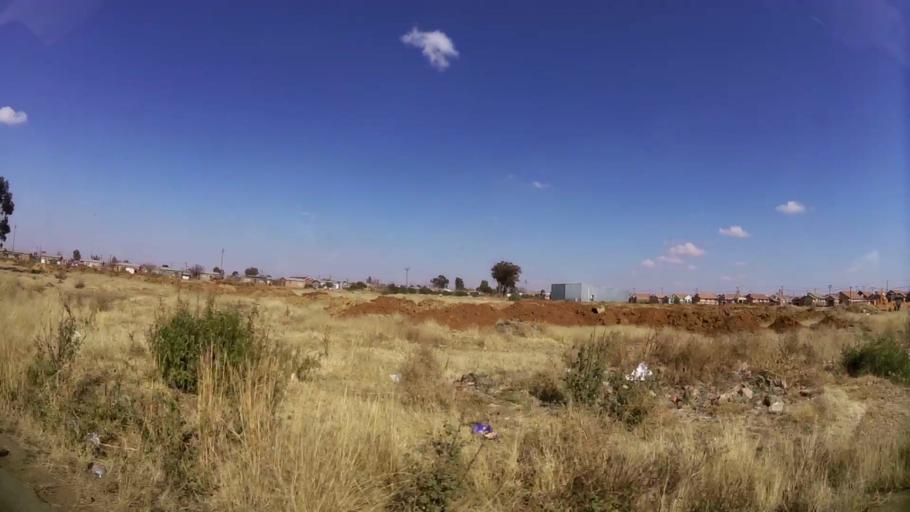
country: ZA
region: Orange Free State
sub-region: Mangaung Metropolitan Municipality
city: Bloemfontein
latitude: -29.1461
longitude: 26.2758
